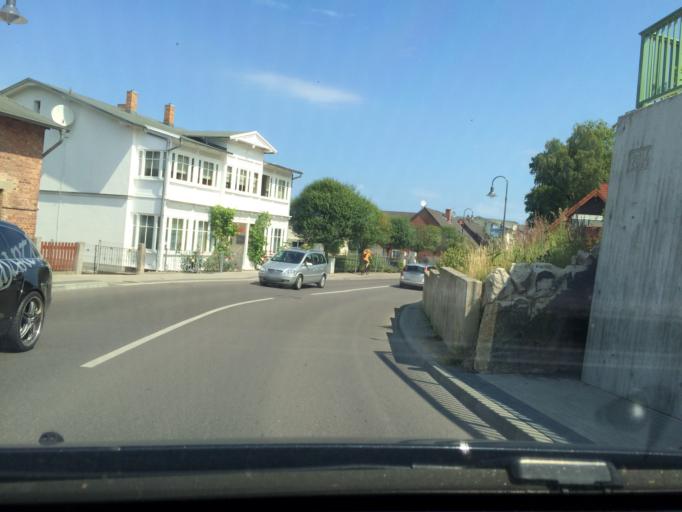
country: DE
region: Mecklenburg-Vorpommern
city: Ostseebad Binz
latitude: 54.3967
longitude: 13.6070
